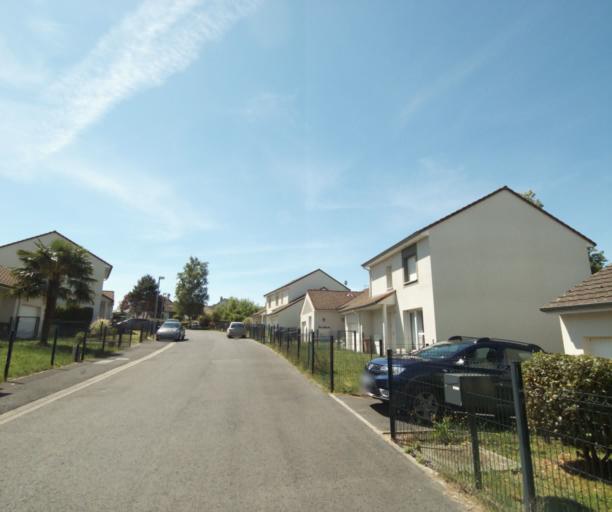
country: FR
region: Champagne-Ardenne
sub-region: Departement des Ardennes
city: La Francheville
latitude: 49.7429
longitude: 4.7143
